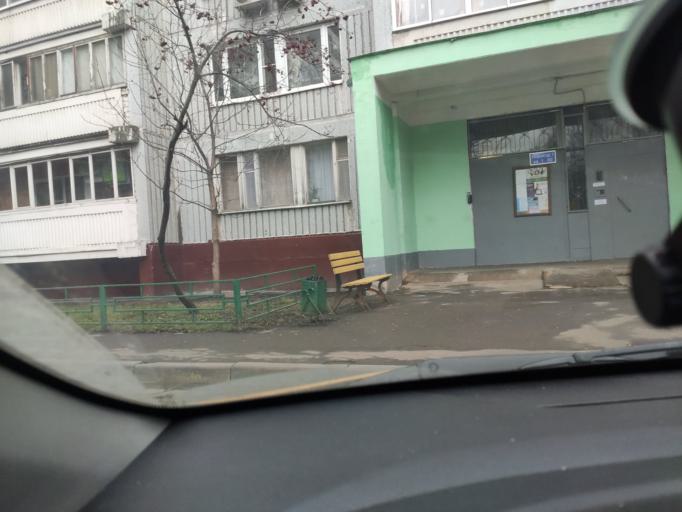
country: RU
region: Moscow
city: Chertanovo Yuzhnoye
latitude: 55.5892
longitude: 37.5948
